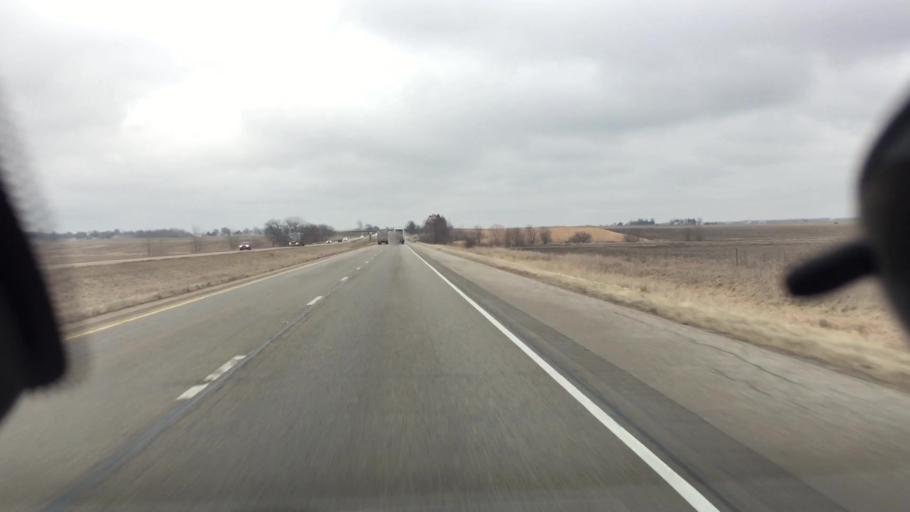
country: US
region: Illinois
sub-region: Tazewell County
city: Mackinaw
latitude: 40.6223
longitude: -89.3583
